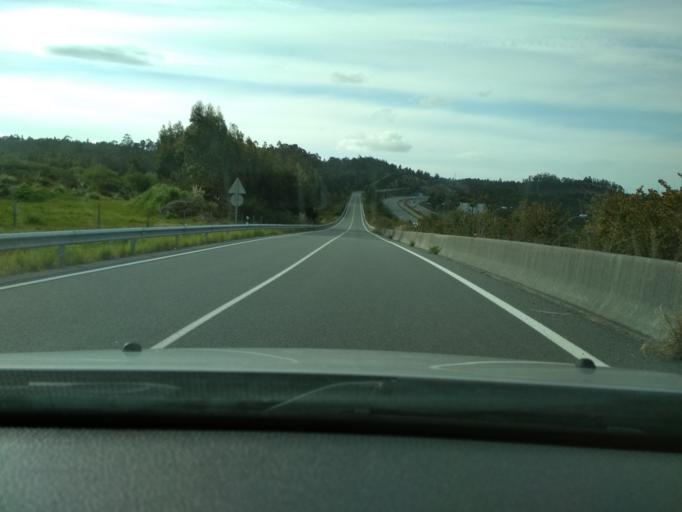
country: ES
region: Galicia
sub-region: Provincia da Coruna
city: Culleredo
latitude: 43.2839
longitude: -8.3957
